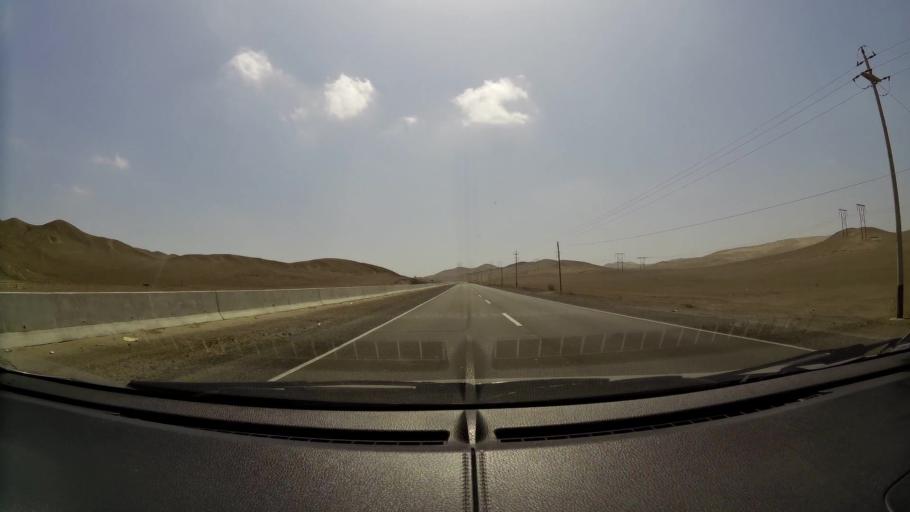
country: PE
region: Ancash
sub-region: Provincia de Huarmey
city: Huarmey
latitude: -10.2006
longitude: -78.0513
